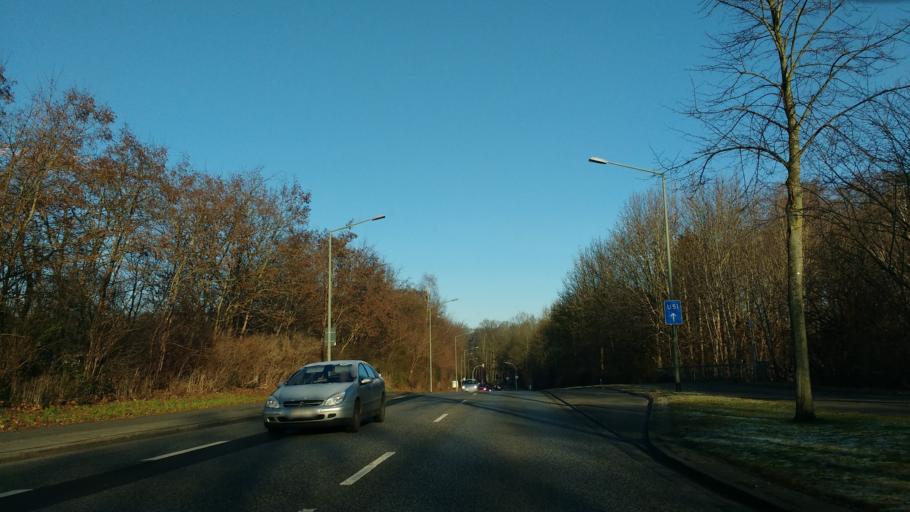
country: DE
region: Schleswig-Holstein
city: Neumunster
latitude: 54.0810
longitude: 9.9612
